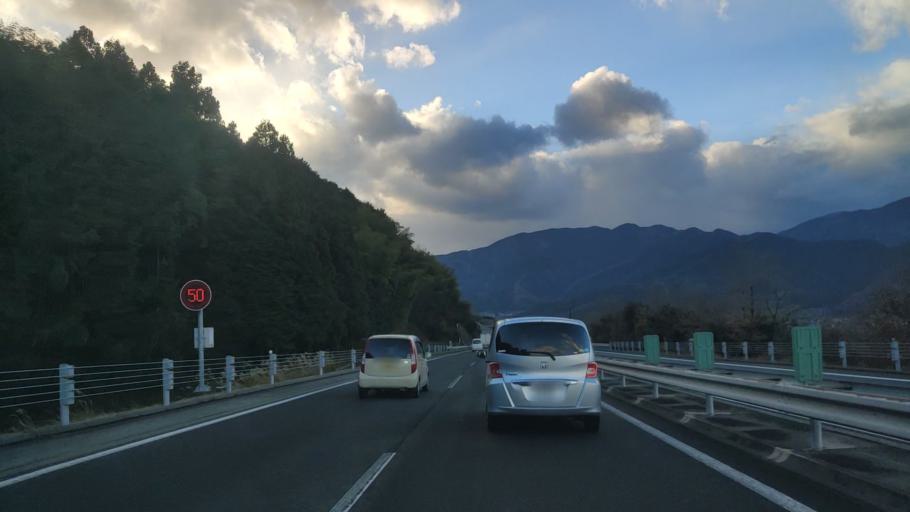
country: JP
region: Ehime
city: Saijo
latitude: 33.8560
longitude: 133.0381
